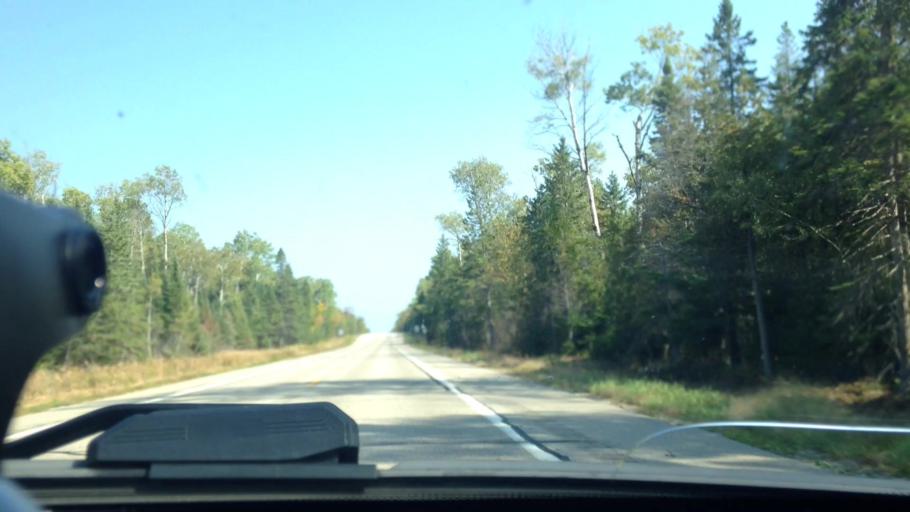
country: US
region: Michigan
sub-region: Luce County
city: Newberry
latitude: 46.3037
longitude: -85.2988
